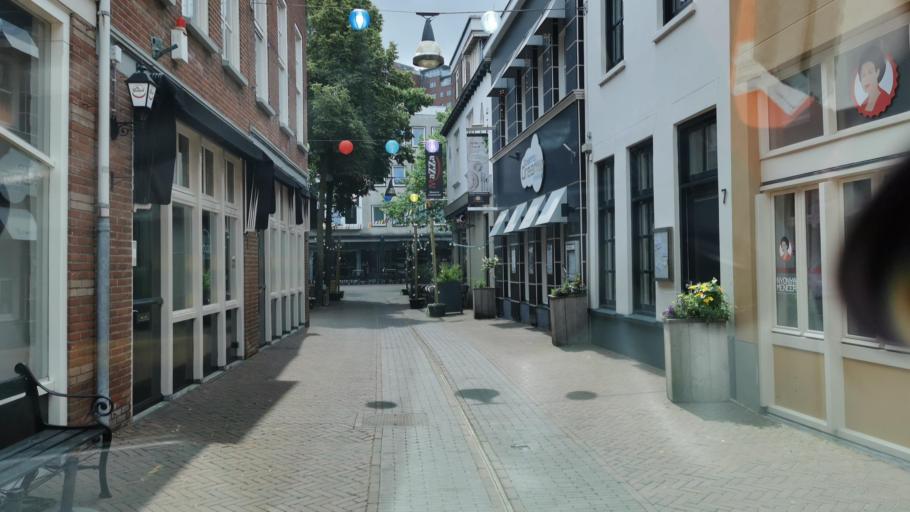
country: NL
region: Overijssel
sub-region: Gemeente Enschede
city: Enschede
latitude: 52.2192
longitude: 6.8949
